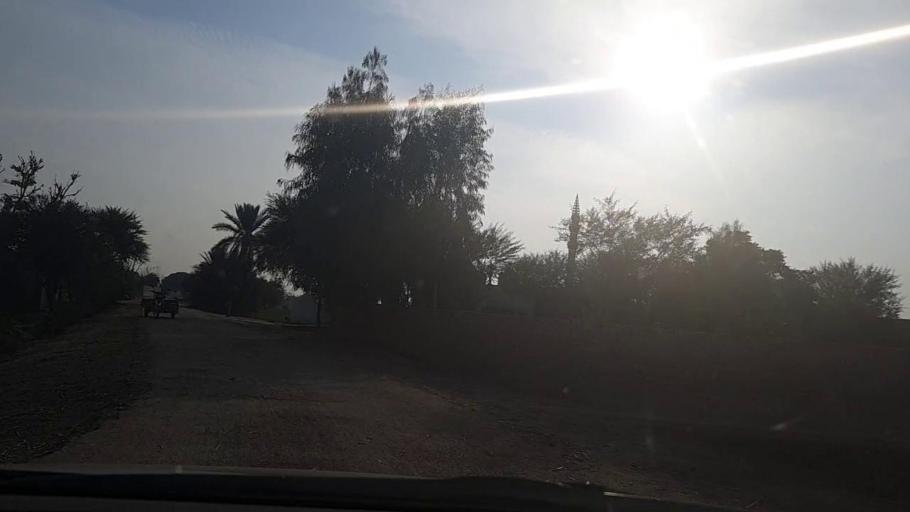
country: PK
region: Sindh
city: Daulatpur
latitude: 26.3338
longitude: 68.0555
